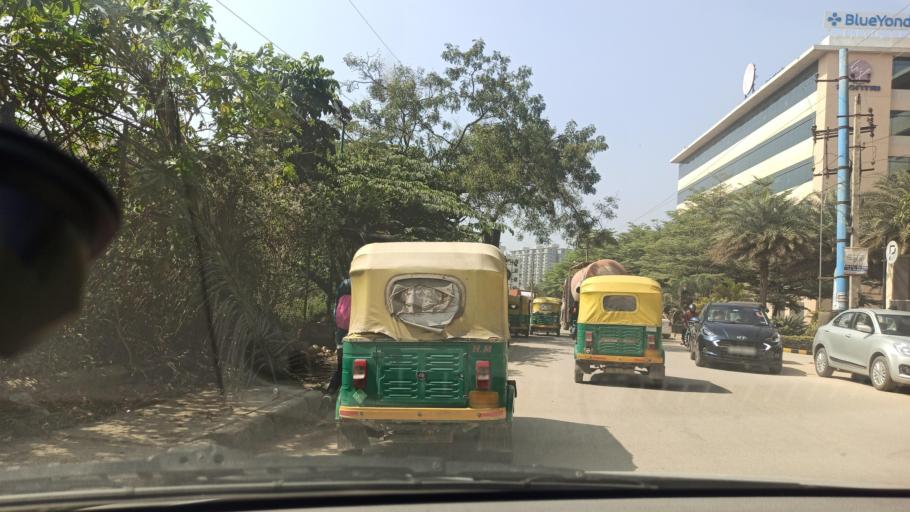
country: IN
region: Karnataka
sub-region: Bangalore Urban
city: Bangalore
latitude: 12.9317
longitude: 77.6845
